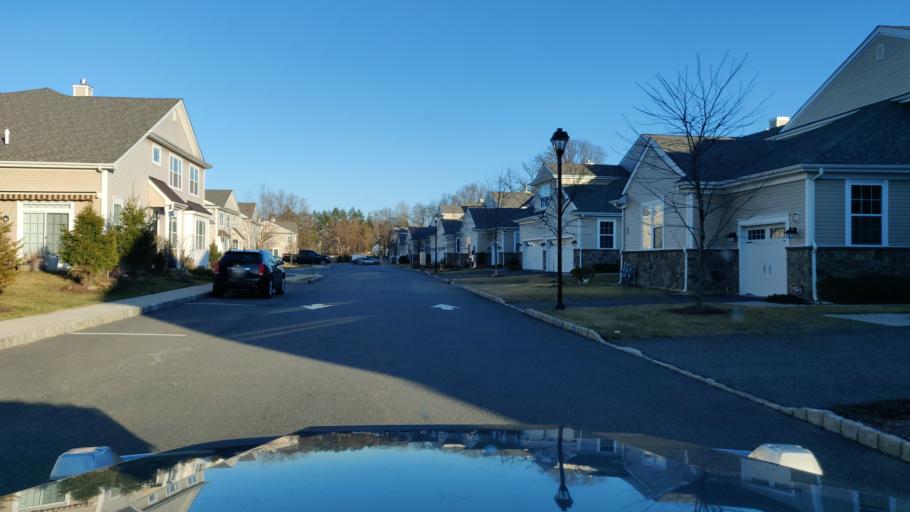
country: US
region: New Jersey
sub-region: Essex County
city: Westville
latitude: 40.8566
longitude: -74.3092
